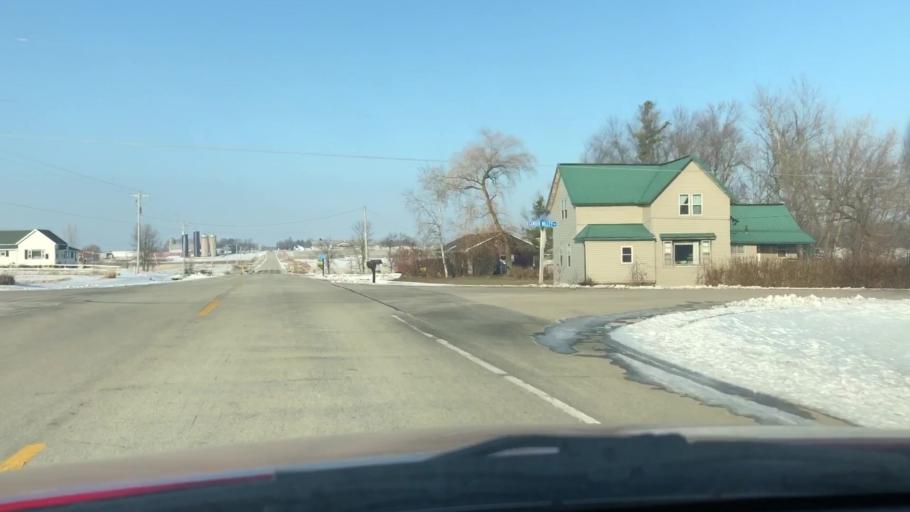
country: US
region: Wisconsin
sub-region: Outagamie County
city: Black Creek
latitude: 44.4014
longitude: -88.3744
